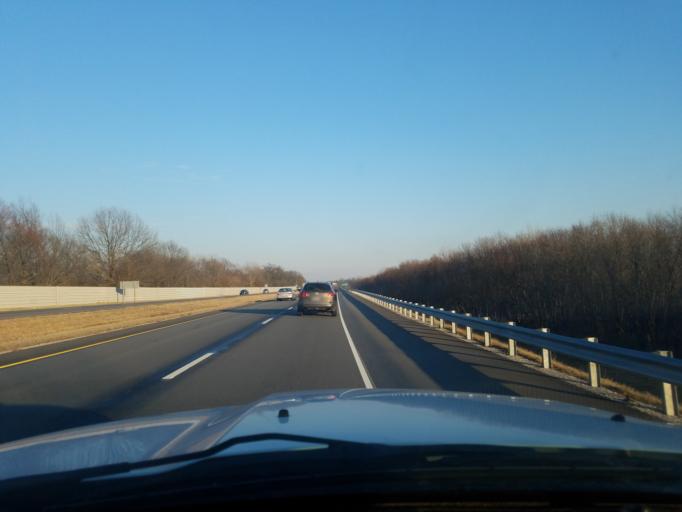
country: US
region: Indiana
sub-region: Vanderburgh County
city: Evansville
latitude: 37.9396
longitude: -87.5115
